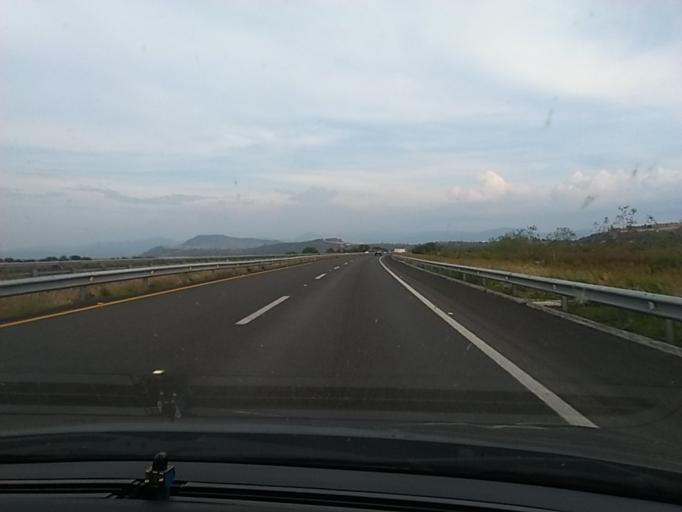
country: MX
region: Michoacan
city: Querendaro
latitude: 19.8889
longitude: -100.9576
